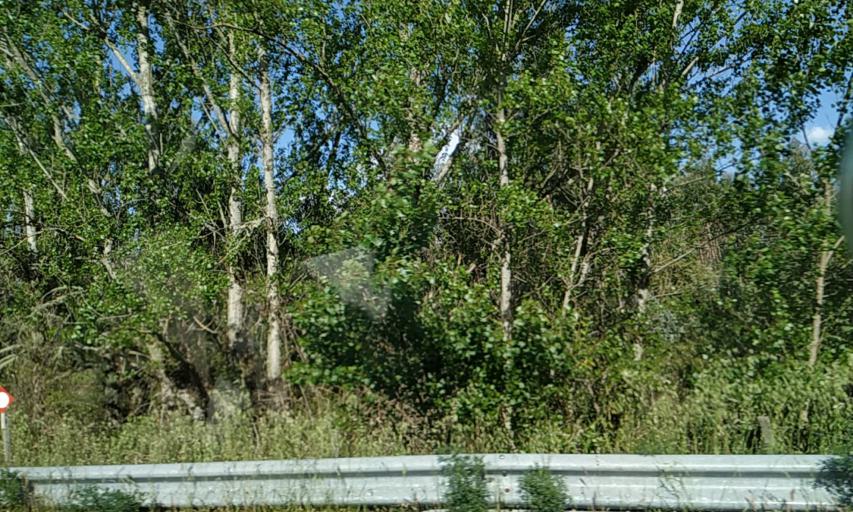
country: PT
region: Portalegre
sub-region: Fronteira
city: Fronteira
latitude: 39.0012
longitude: -7.4682
